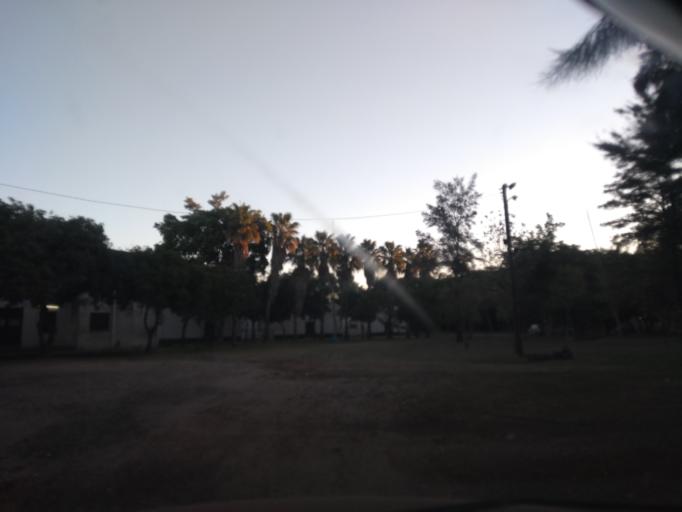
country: AR
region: Chaco
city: Fontana
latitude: -27.4248
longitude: -59.0044
